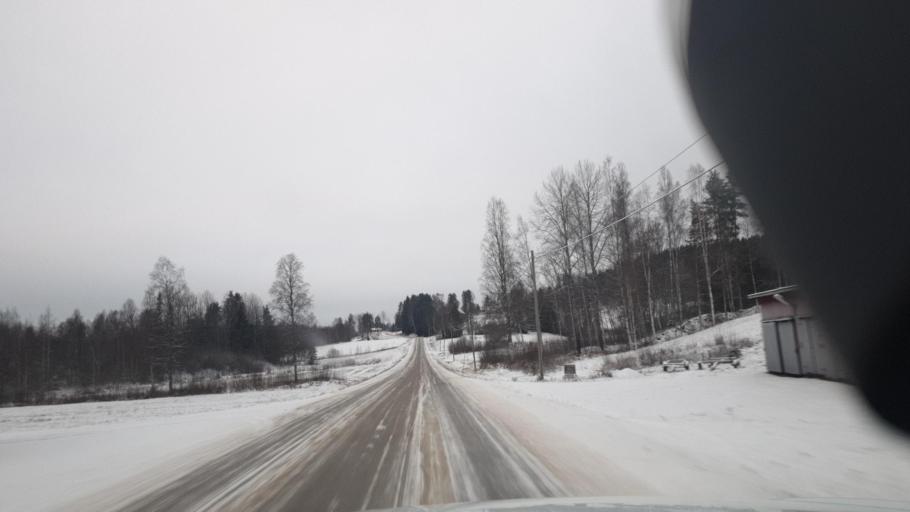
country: SE
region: Vaermland
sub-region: Eda Kommun
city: Amotfors
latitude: 59.9102
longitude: 12.5237
